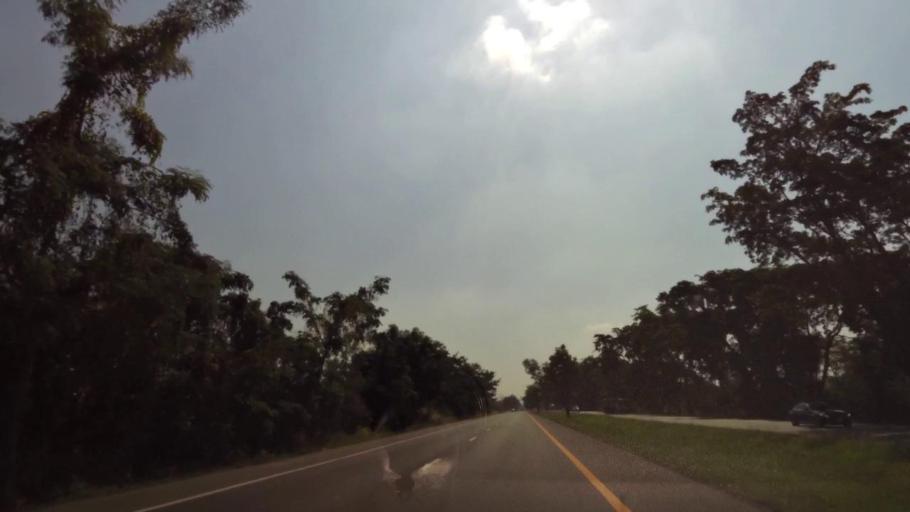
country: TH
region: Phichit
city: Bueng Na Rang
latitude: 16.2080
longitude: 100.1274
